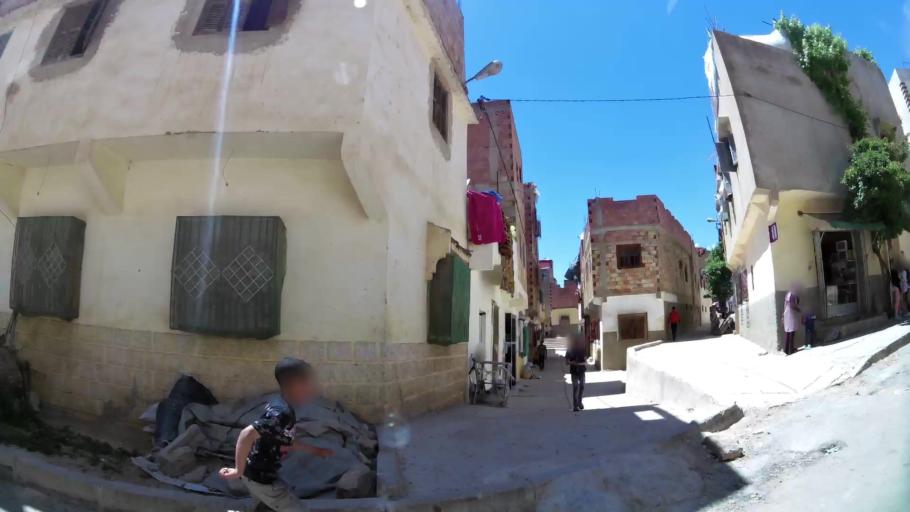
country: MA
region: Meknes-Tafilalet
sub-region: Meknes
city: Meknes
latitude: 33.9074
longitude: -5.5788
